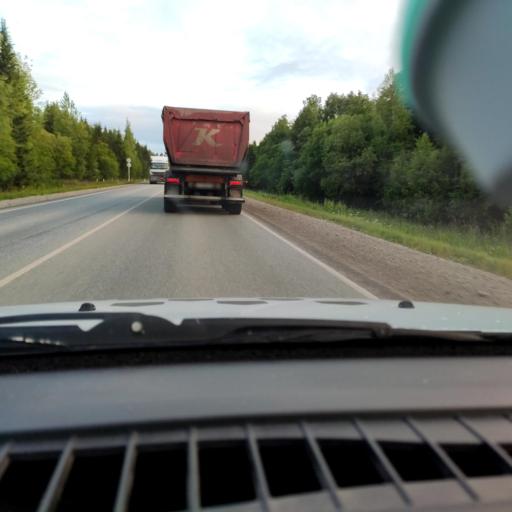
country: RU
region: Perm
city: Polazna
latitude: 58.3029
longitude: 56.6177
